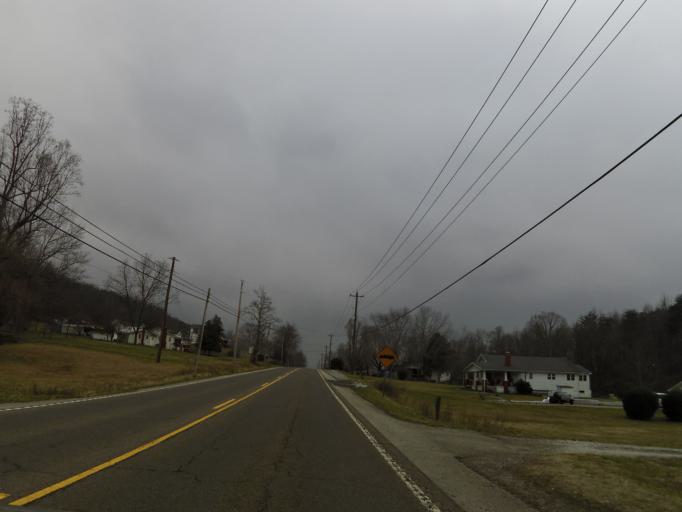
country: US
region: Tennessee
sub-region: Anderson County
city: Rocky Top
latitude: 36.1923
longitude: -84.1448
